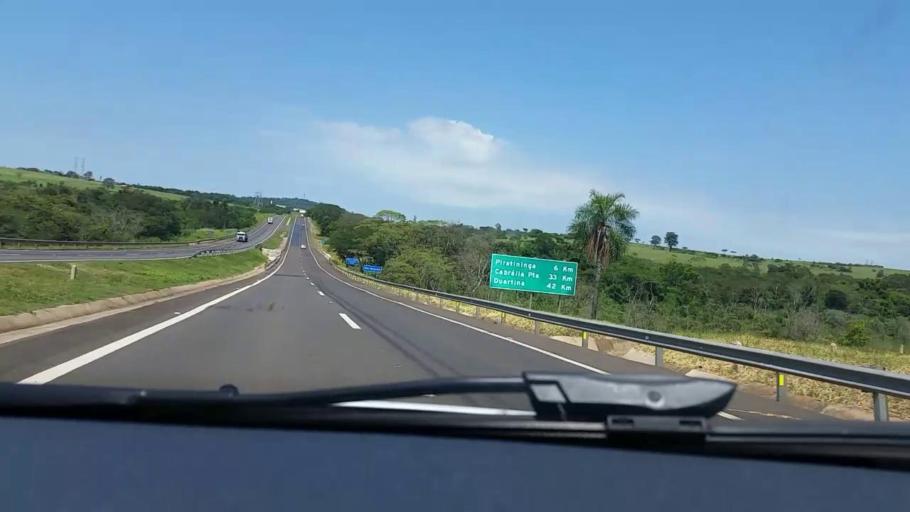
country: BR
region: Sao Paulo
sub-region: Bauru
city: Bauru
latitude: -22.4054
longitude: -49.0961
